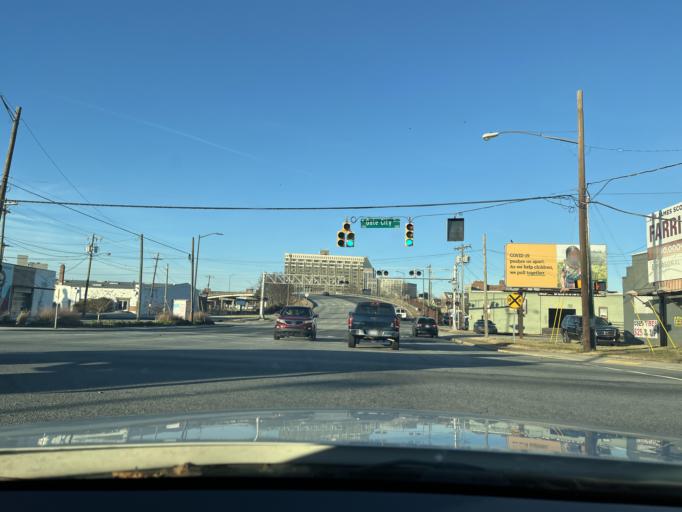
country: US
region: North Carolina
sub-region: Guilford County
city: Greensboro
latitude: 36.0647
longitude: -79.7929
